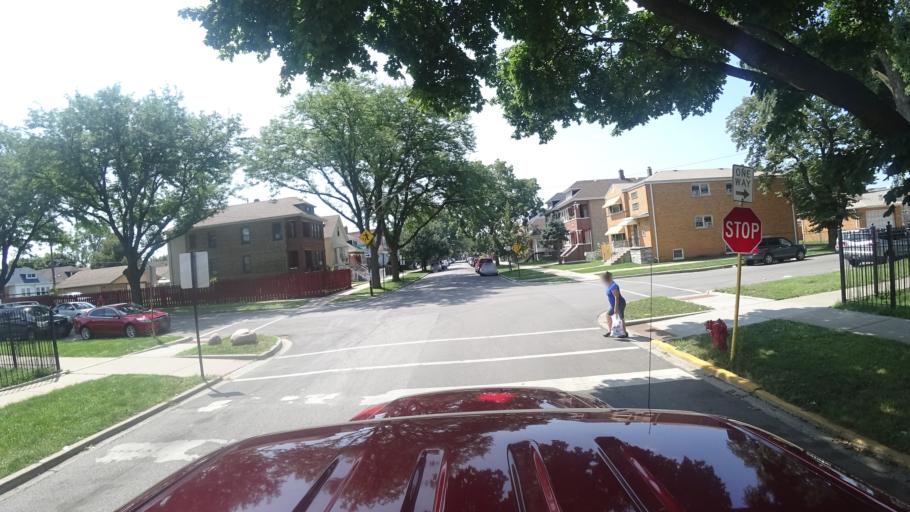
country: US
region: Illinois
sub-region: Cook County
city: Cicero
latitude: 41.7992
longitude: -87.7025
